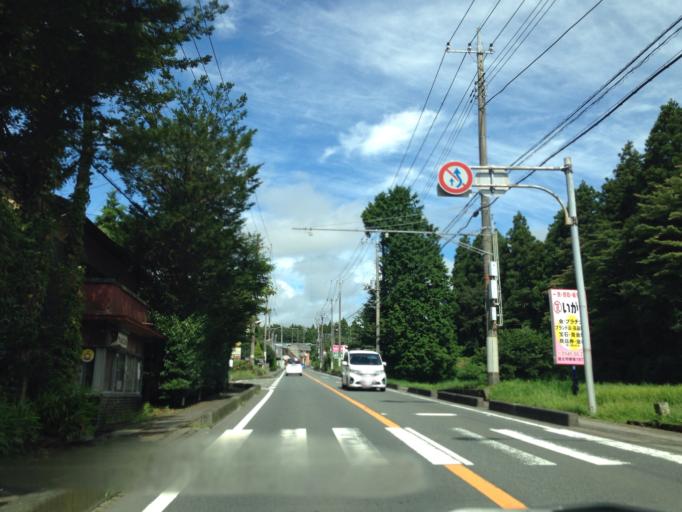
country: JP
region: Shizuoka
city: Gotemba
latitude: 35.3364
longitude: 138.8949
